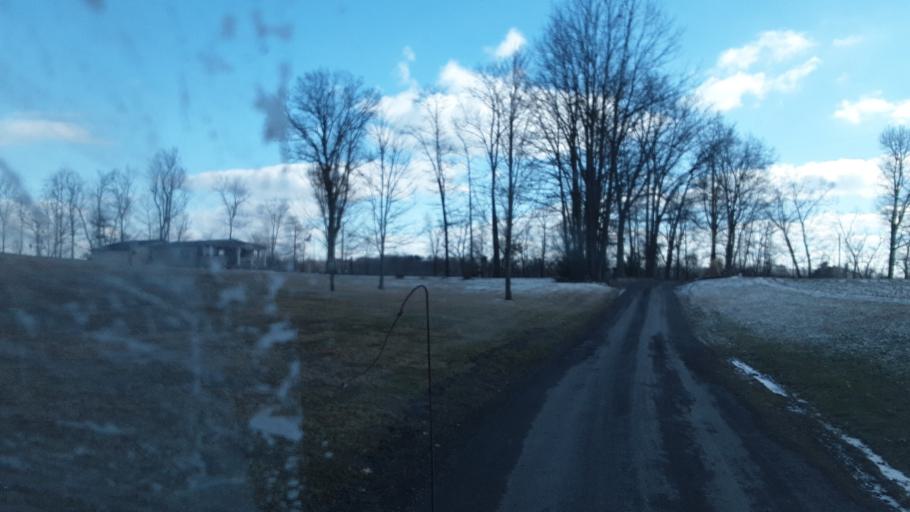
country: US
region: Ohio
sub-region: Carroll County
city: Carrollton
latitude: 40.5464
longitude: -81.0726
